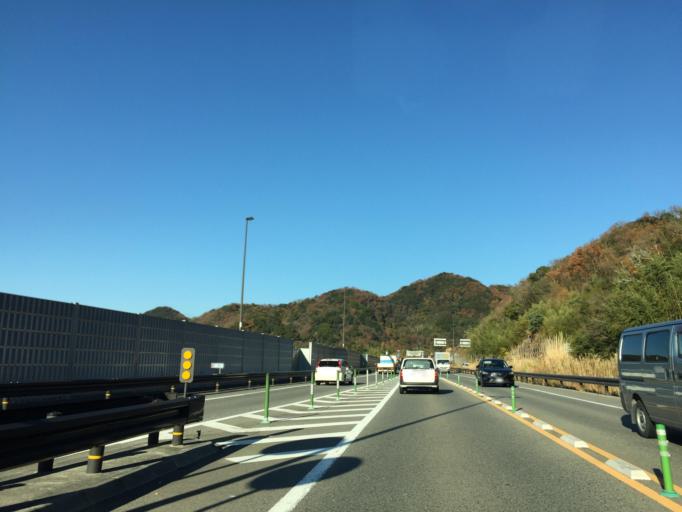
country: JP
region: Wakayama
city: Wakayama-shi
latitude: 34.2613
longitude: 135.1719
